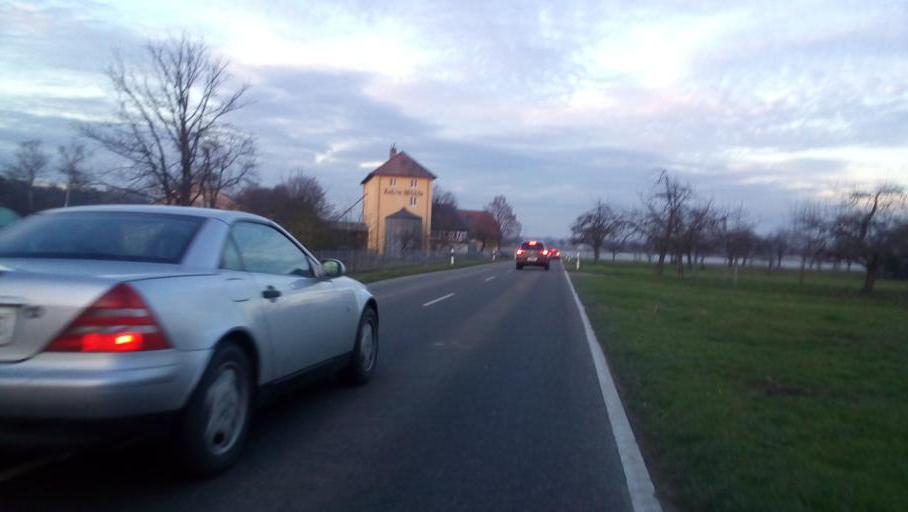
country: DE
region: Baden-Wuerttemberg
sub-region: Karlsruhe Region
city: Zell
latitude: 48.6956
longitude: 8.0658
